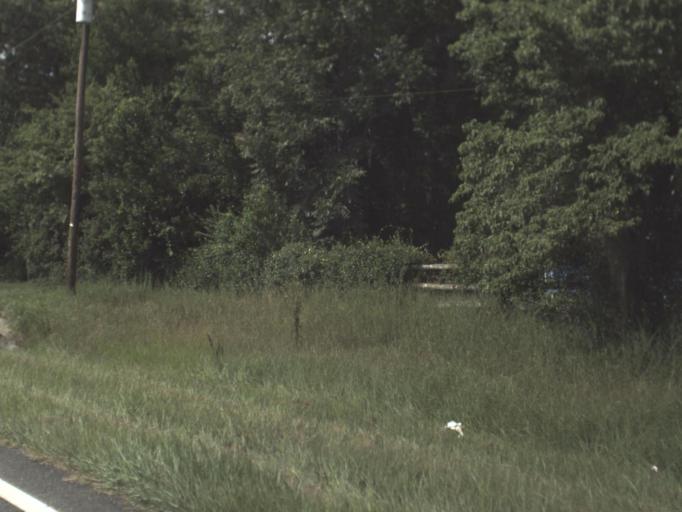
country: US
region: Florida
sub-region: Taylor County
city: Perry
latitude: 30.3589
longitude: -83.6547
